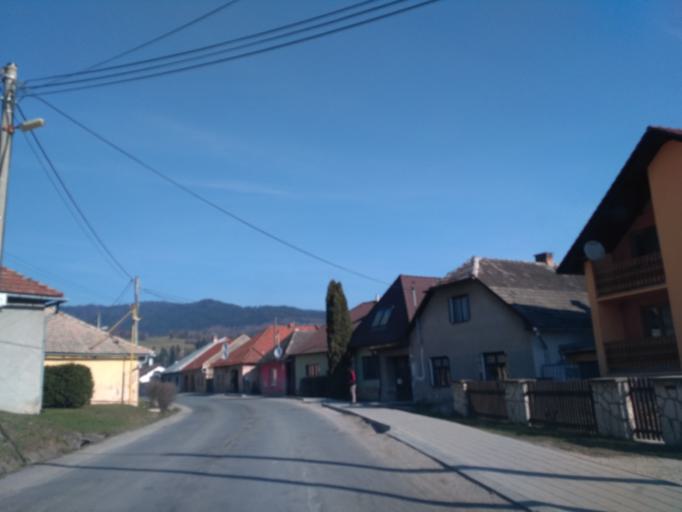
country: SK
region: Kosicky
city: Krompachy
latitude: 48.8025
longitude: 20.8063
